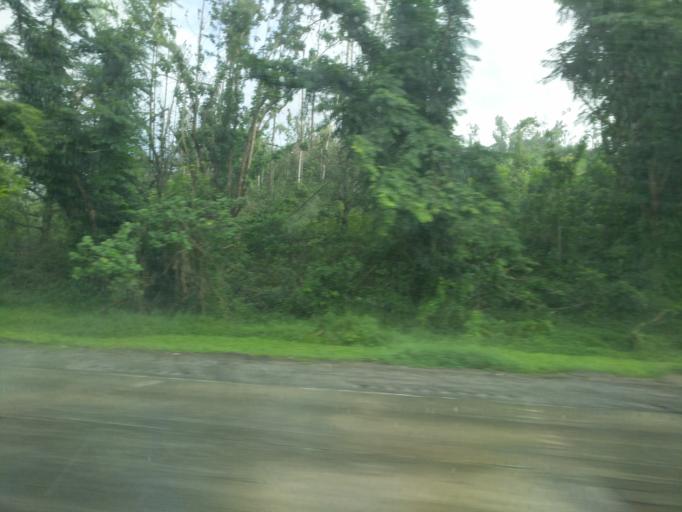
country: PR
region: Cidra
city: Bayamon
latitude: 18.1633
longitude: -66.0897
